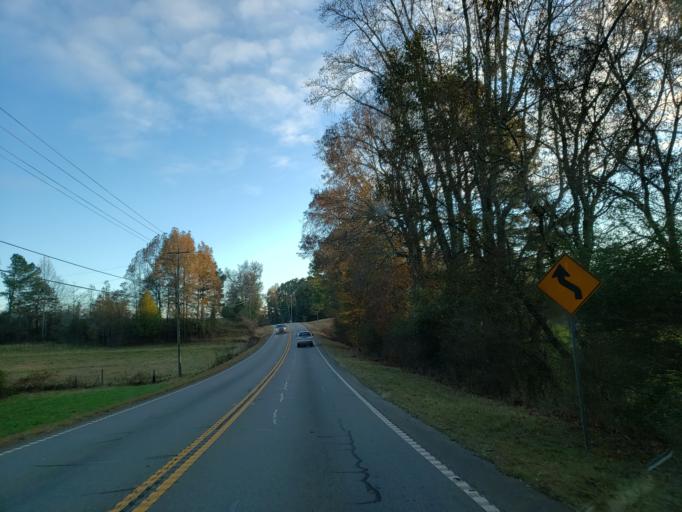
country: US
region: Georgia
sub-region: Fulton County
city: Milton
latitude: 34.2502
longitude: -84.2857
